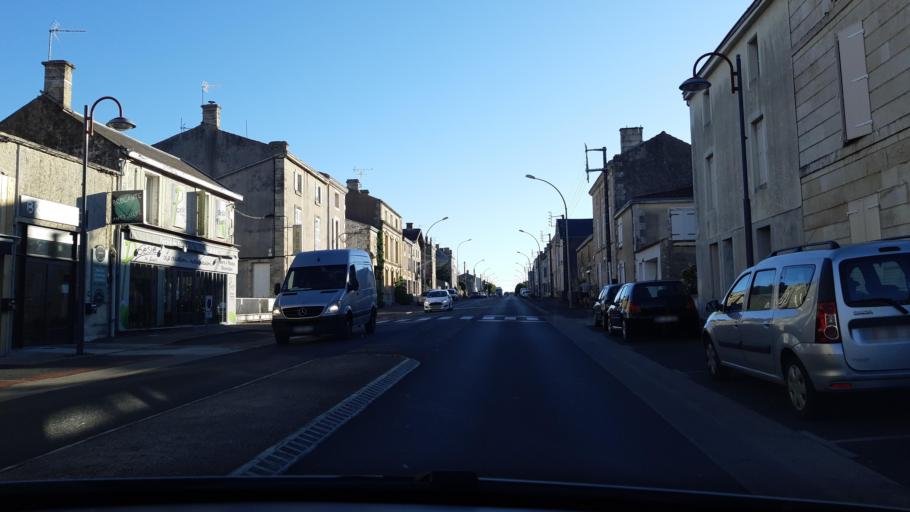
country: FR
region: Poitou-Charentes
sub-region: Departement des Deux-Sevres
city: La Creche
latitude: 46.3628
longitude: -0.2980
